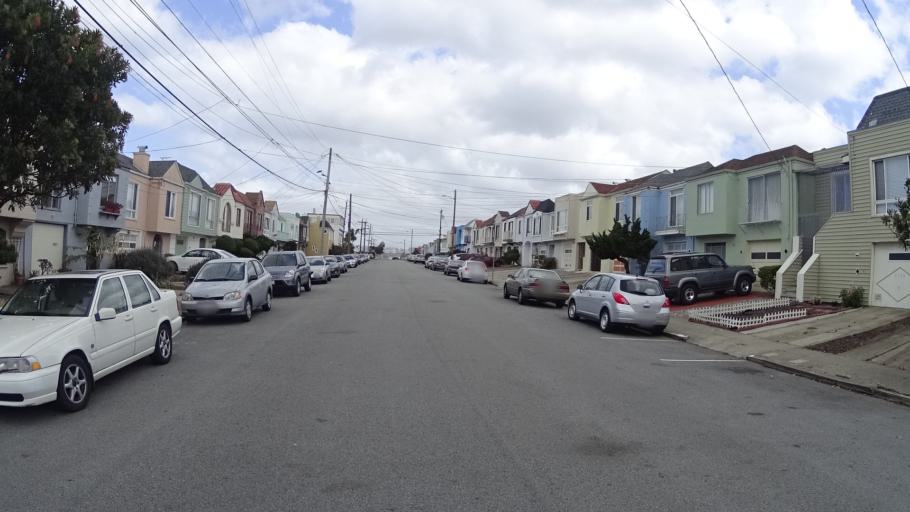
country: US
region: California
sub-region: San Mateo County
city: Daly City
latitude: 37.7426
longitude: -122.5025
